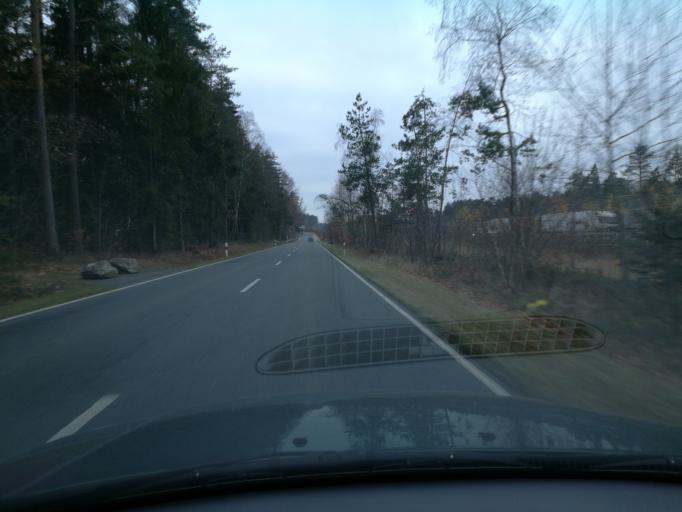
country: DE
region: Bavaria
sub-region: Regierungsbezirk Mittelfranken
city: Feucht
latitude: 49.3917
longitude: 11.1819
